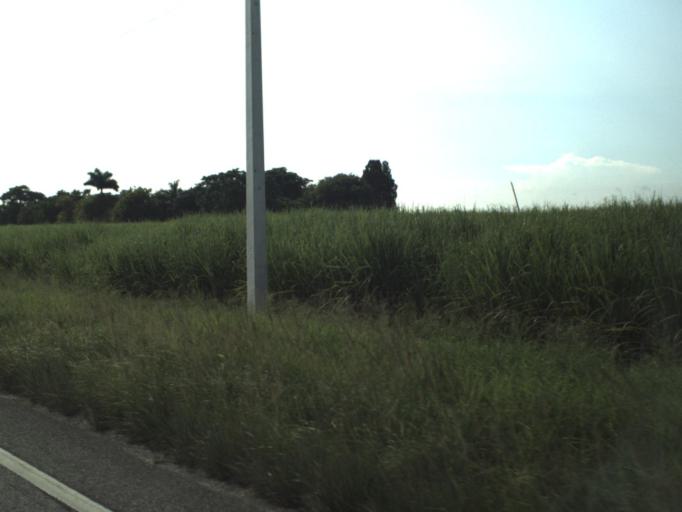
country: US
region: Florida
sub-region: Palm Beach County
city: South Bay
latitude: 26.6807
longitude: -80.7434
